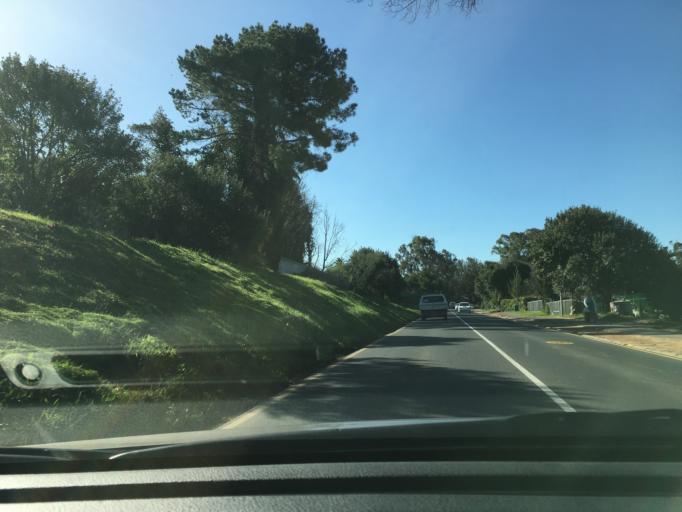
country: ZA
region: Western Cape
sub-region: City of Cape Town
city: Constantia
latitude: -34.0235
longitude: 18.4363
